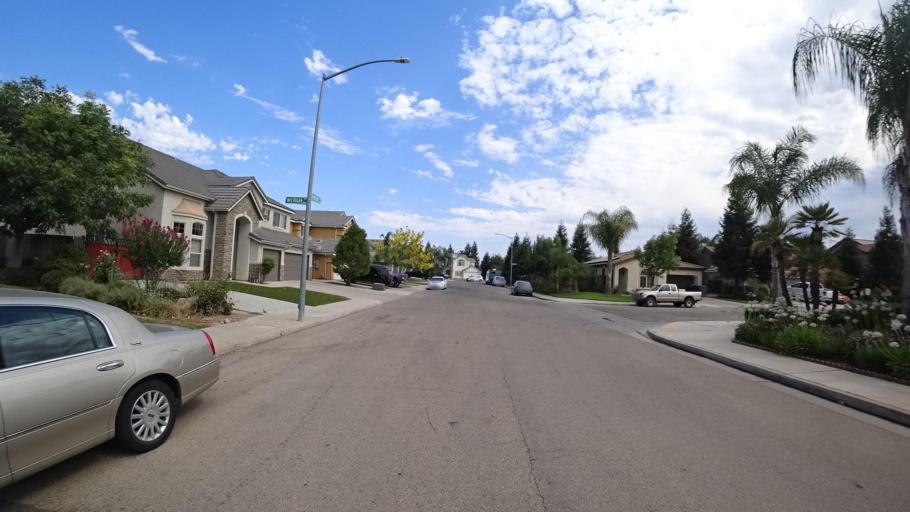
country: US
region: California
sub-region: Fresno County
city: Tarpey Village
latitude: 36.7766
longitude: -119.6680
